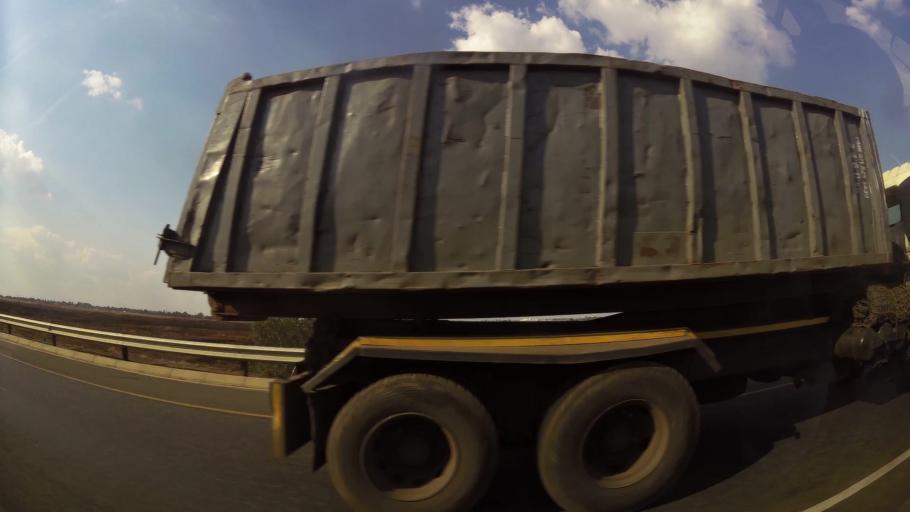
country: ZA
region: Gauteng
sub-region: Ekurhuleni Metropolitan Municipality
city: Brakpan
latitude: -26.2917
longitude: 28.3338
